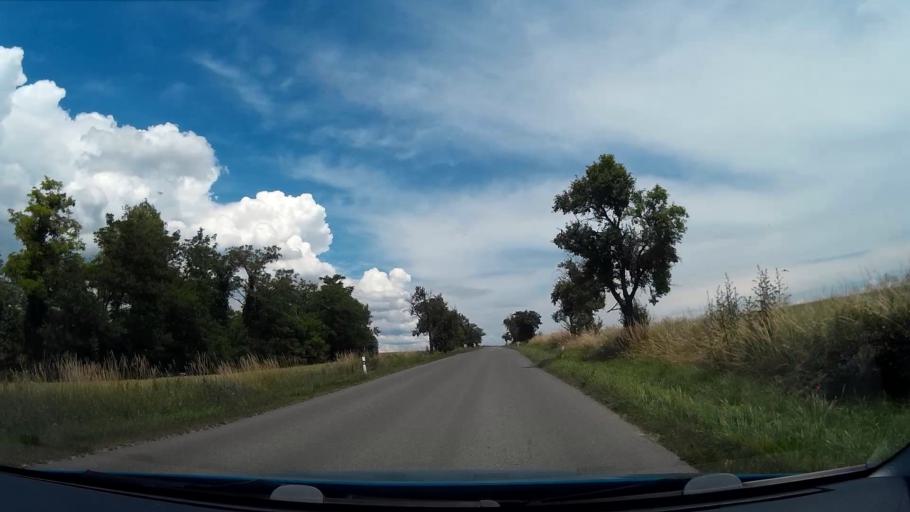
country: CZ
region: South Moravian
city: Orechov
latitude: 49.0682
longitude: 16.5259
